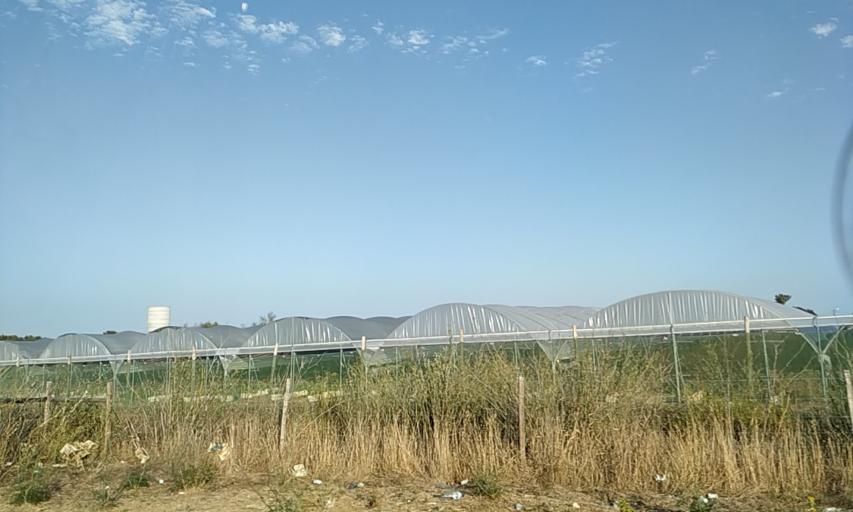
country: PT
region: Santarem
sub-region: Alcanena
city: Alcanena
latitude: 39.4309
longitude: -8.6320
